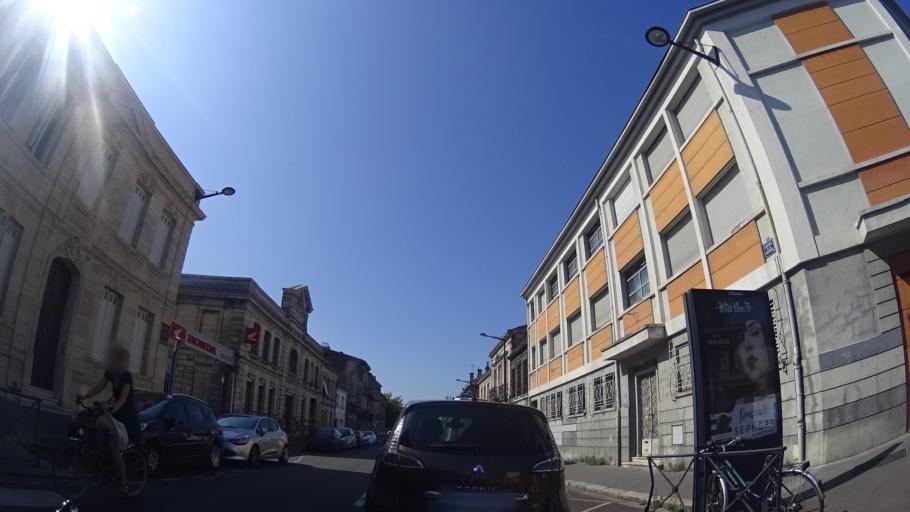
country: FR
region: Aquitaine
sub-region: Departement de la Gironde
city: Bordeaux
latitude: 44.8222
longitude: -0.5725
